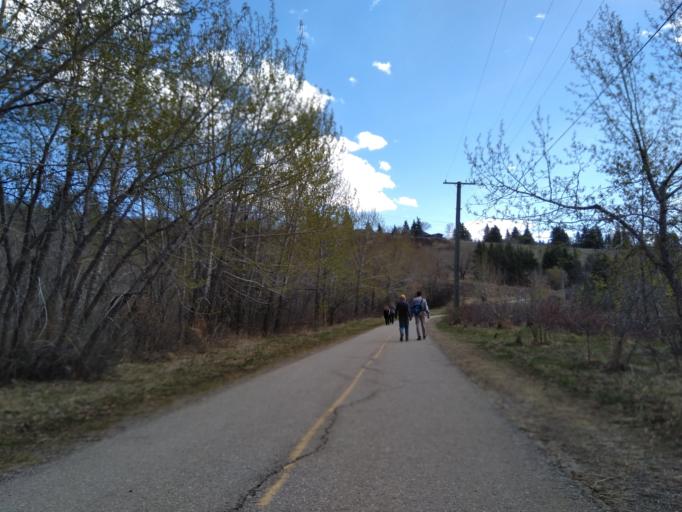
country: CA
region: Alberta
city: Calgary
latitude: 51.0853
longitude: -114.1677
